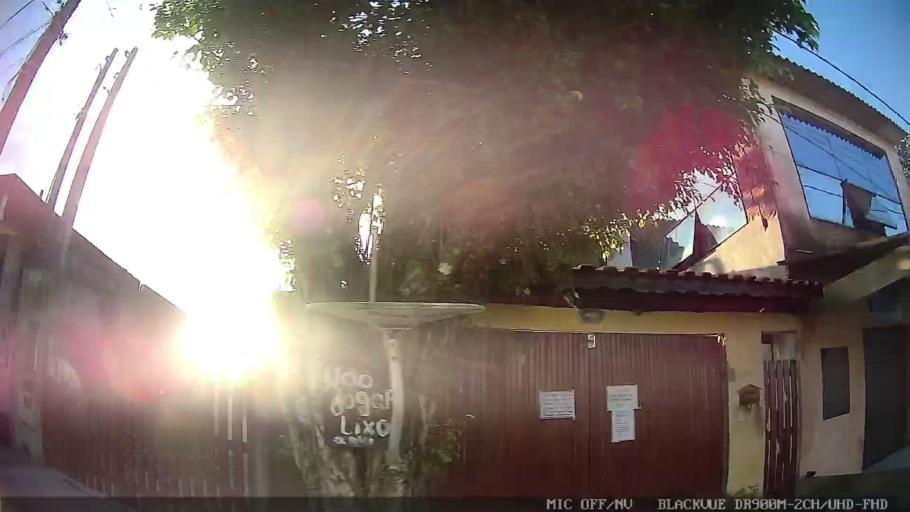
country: BR
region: Sao Paulo
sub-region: Itanhaem
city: Itanhaem
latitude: -24.1385
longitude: -46.7240
